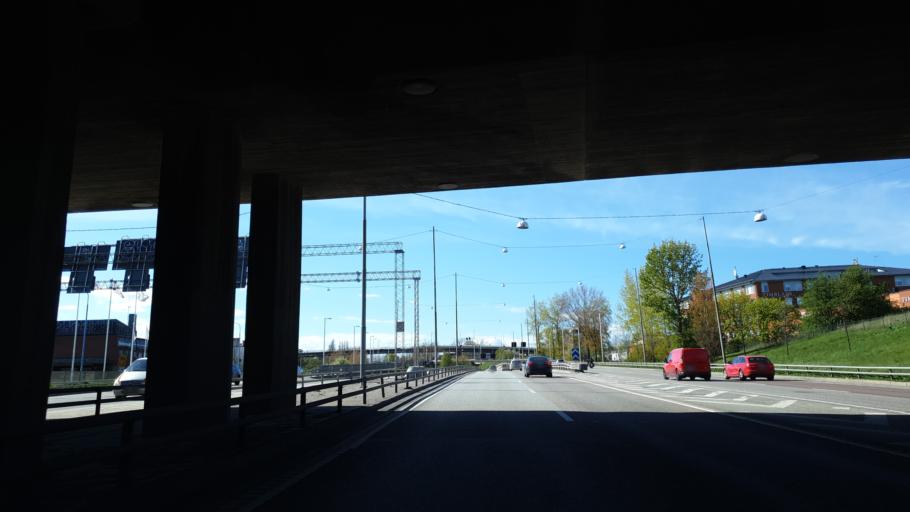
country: SE
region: Stockholm
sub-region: Stockholms Kommun
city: Arsta
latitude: 59.2983
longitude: 18.0269
